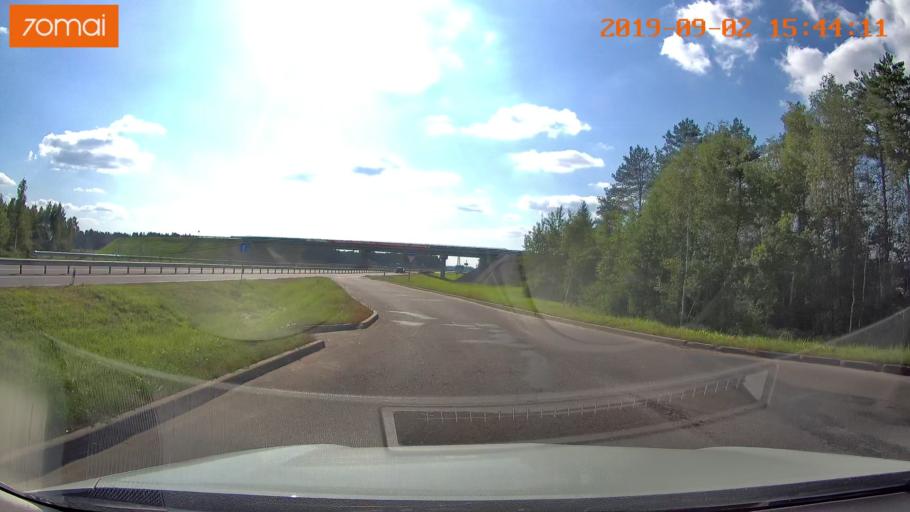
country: BY
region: Mogilev
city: Byalynichy
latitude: 53.9090
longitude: 29.4079
